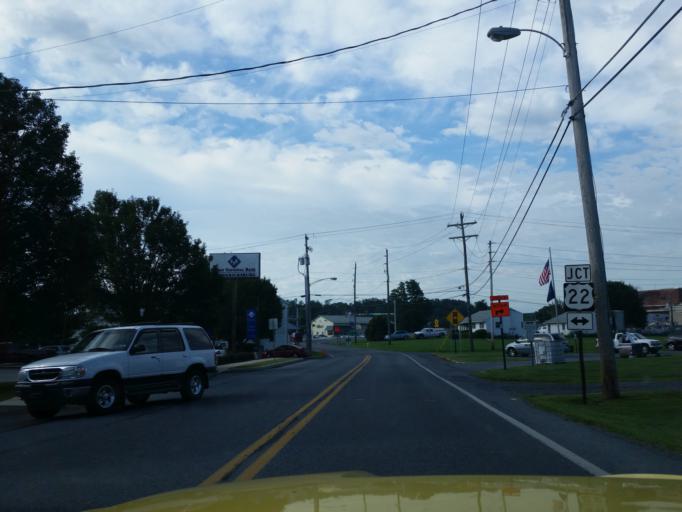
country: US
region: Pennsylvania
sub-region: Lebanon County
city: Fredericksburg
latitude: 40.4412
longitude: -76.4298
